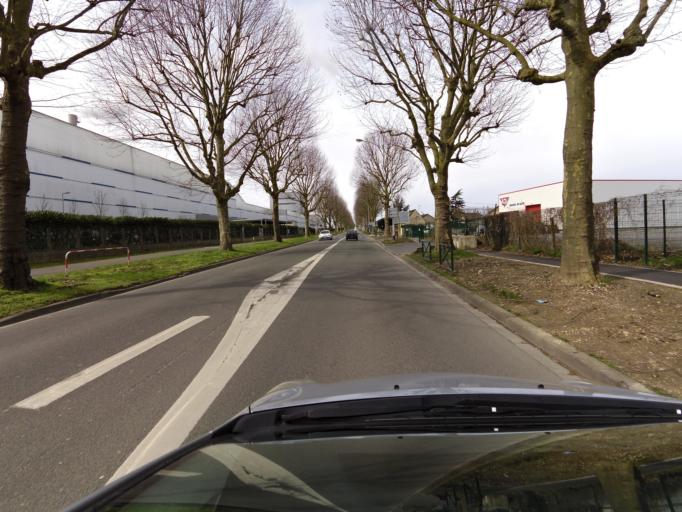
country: FR
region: Ile-de-France
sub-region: Departement de Seine-et-Marne
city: Villeparisis
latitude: 48.9380
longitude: 2.5973
